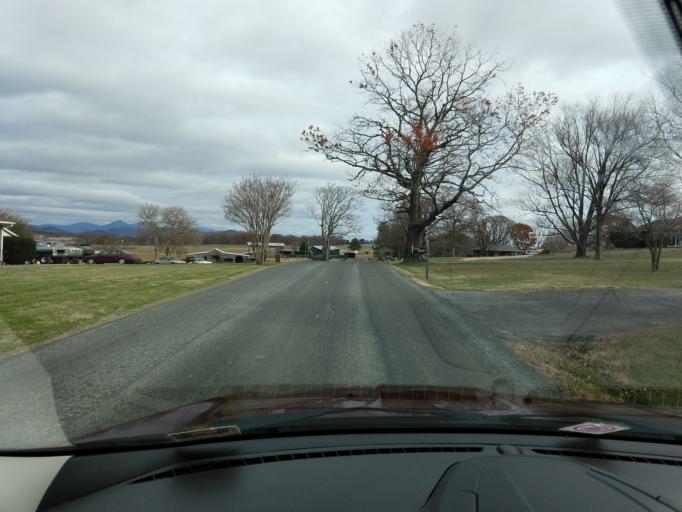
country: US
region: Virginia
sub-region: Franklin County
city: North Shore
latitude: 37.2125
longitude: -79.6781
